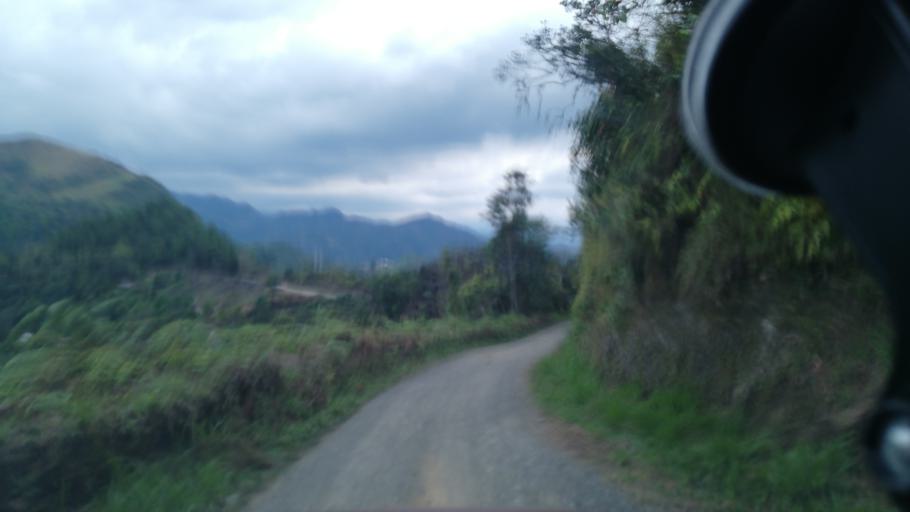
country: CO
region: Cundinamarca
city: Vergara
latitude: 5.1693
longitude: -74.2625
